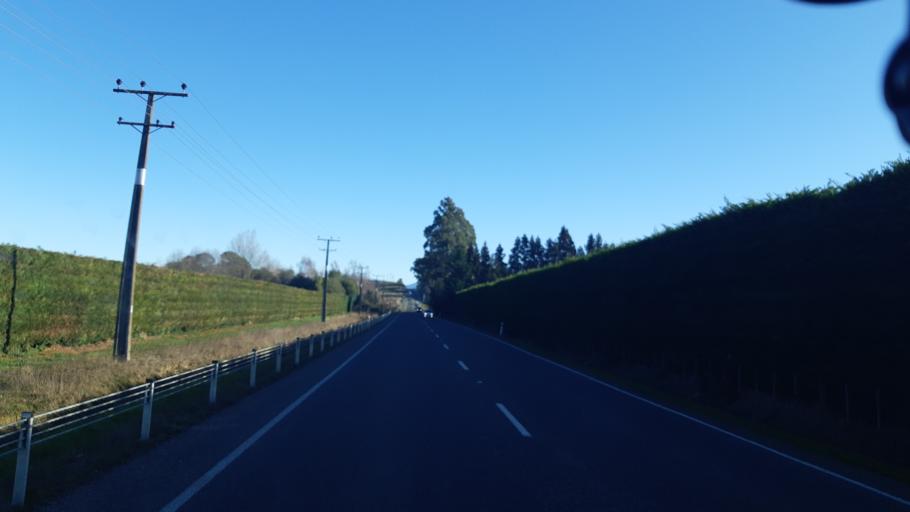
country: NZ
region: Tasman
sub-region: Tasman District
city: Mapua
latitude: -41.3008
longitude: 173.1103
